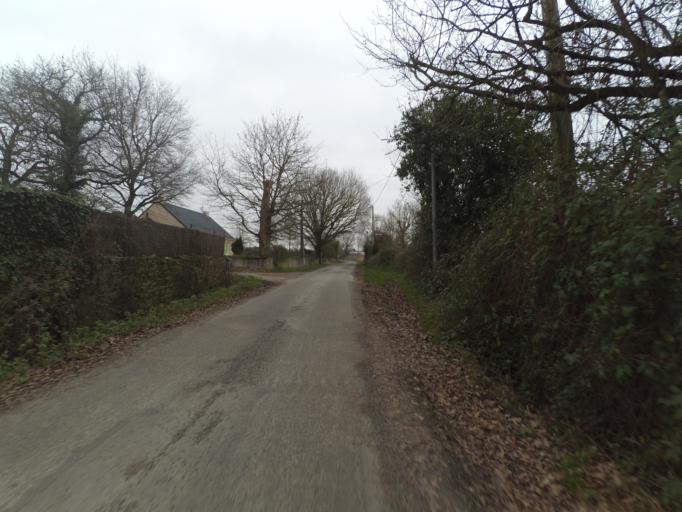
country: FR
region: Pays de la Loire
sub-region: Departement de la Loire-Atlantique
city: Coueron
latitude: 47.2380
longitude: -1.7043
